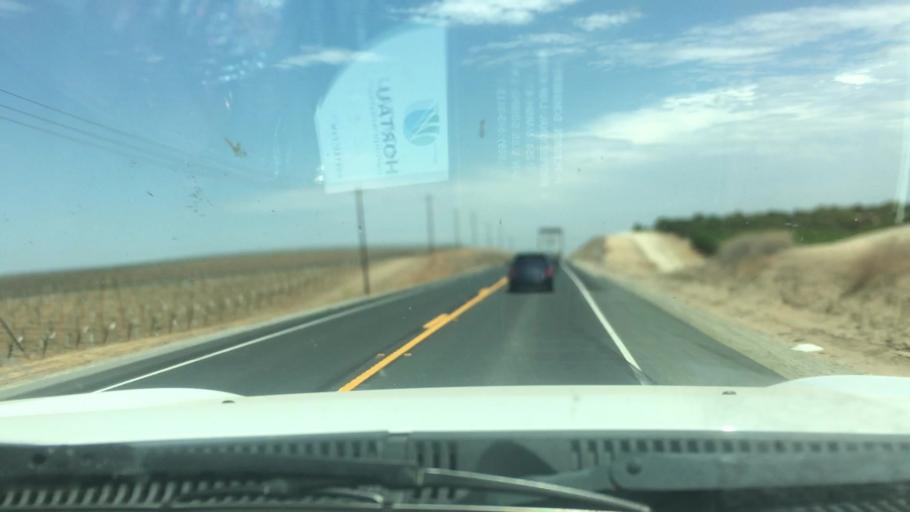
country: US
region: California
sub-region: Tulare County
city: Richgrove
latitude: 35.7840
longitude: -119.0534
